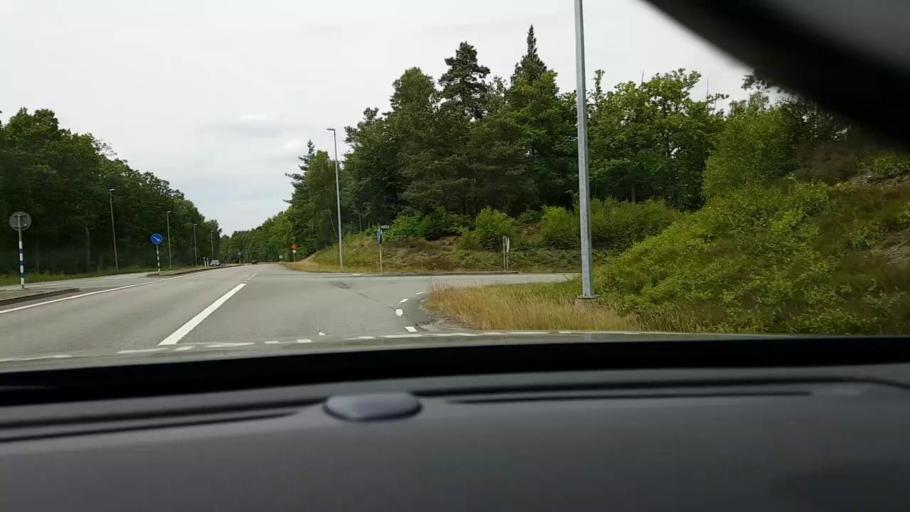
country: SE
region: Skane
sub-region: Hassleholms Kommun
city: Hassleholm
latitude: 56.1644
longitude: 13.7329
